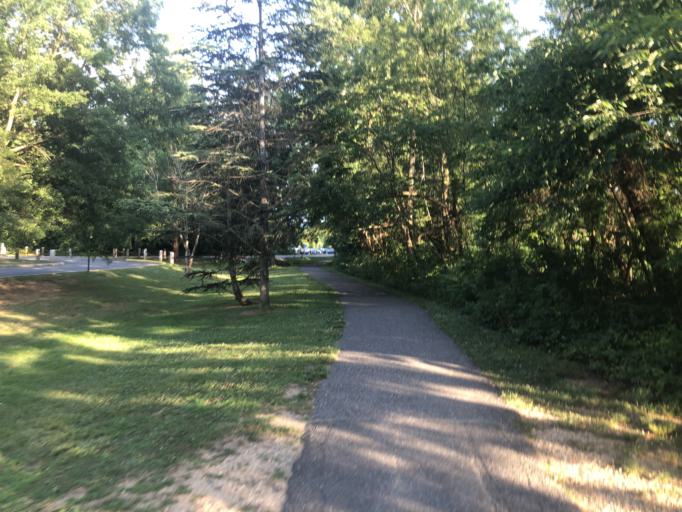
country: US
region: Maryland
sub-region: Harford County
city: Joppatowne
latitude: 39.4009
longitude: -76.3511
